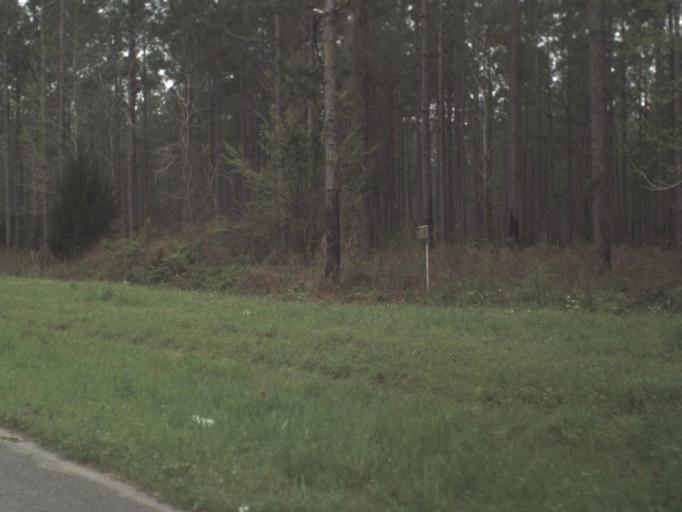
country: US
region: Florida
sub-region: Gadsden County
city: Gretna
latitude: 30.5542
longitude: -84.6770
